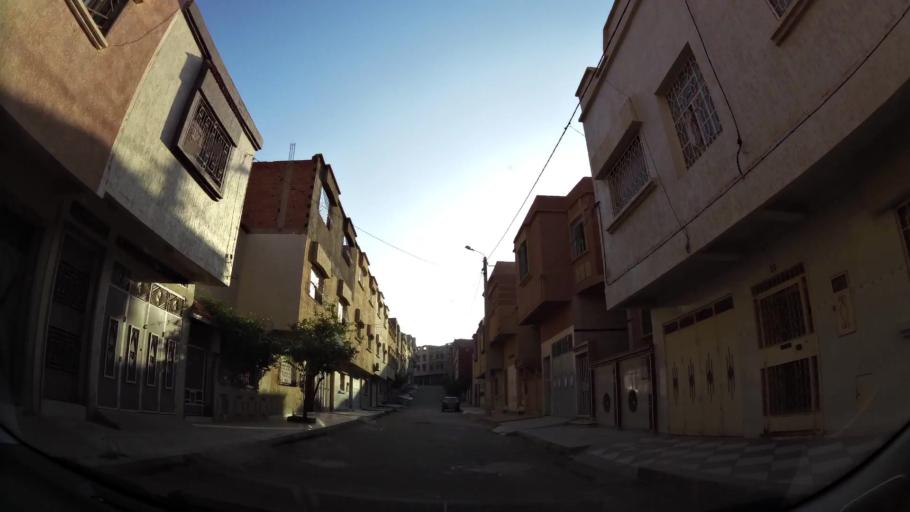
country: MA
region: Oriental
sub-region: Oujda-Angad
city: Oujda
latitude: 34.6746
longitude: -1.9402
